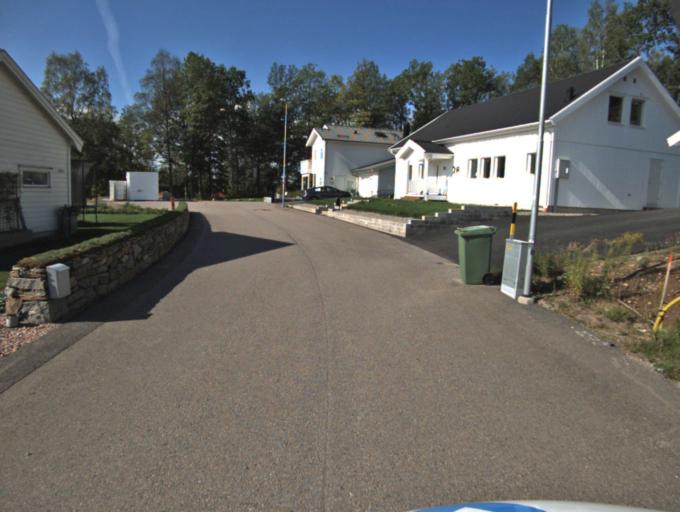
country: SE
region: Vaestra Goetaland
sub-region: Ulricehamns Kommun
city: Ulricehamn
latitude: 57.8072
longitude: 13.3985
